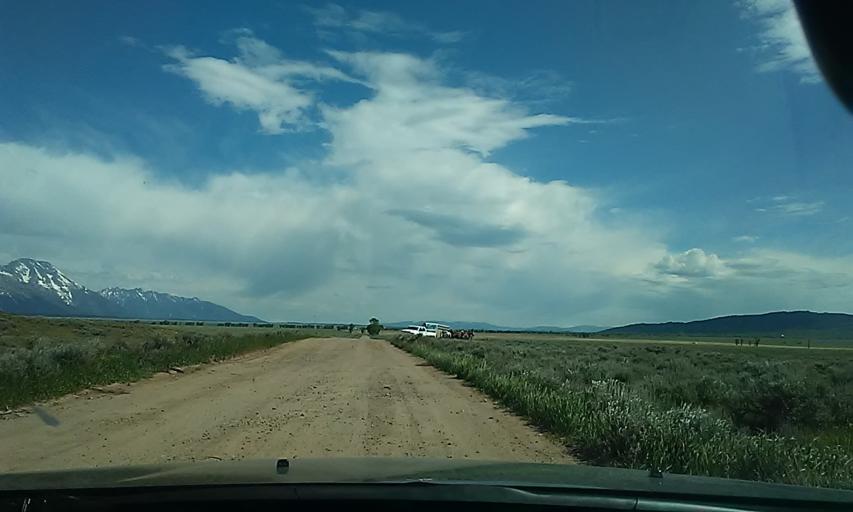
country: US
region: Wyoming
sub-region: Teton County
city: Jackson
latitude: 43.6254
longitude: -110.6643
